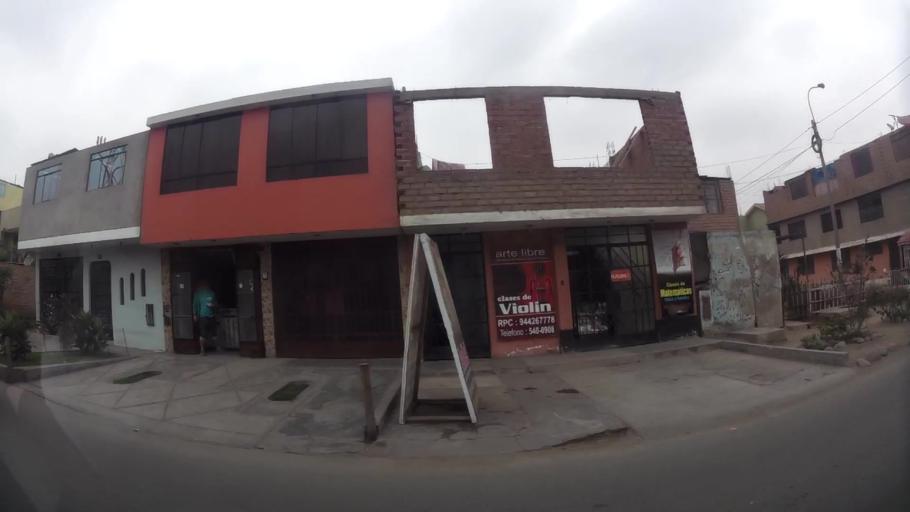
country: PE
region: Lima
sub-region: Lima
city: Independencia
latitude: -11.9391
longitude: -77.0855
